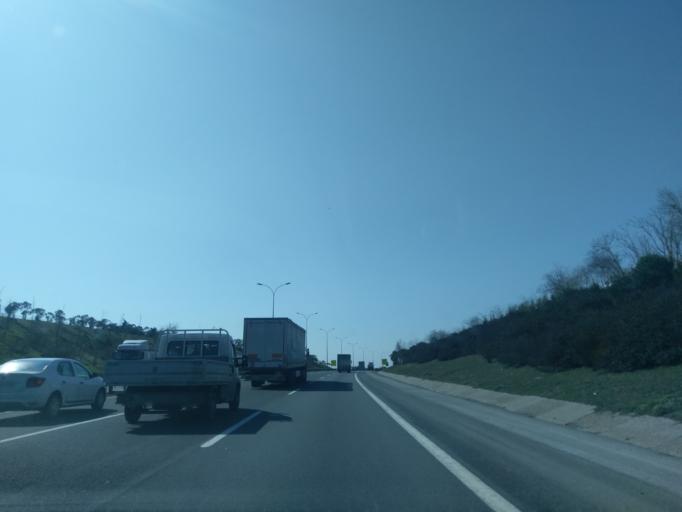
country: TR
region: Istanbul
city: Celaliye
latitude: 41.0531
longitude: 28.4529
